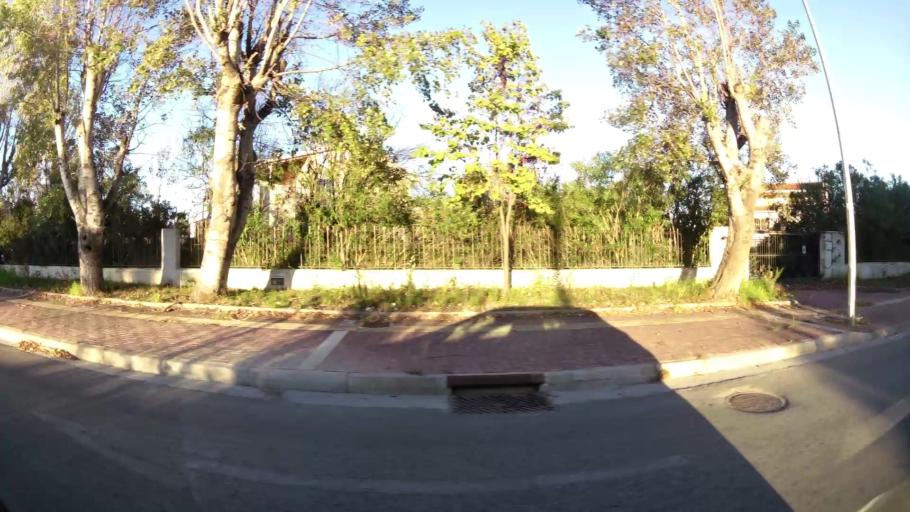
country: GR
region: Attica
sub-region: Nomarchia Anatolikis Attikis
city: Spata
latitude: 37.9692
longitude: 23.9061
